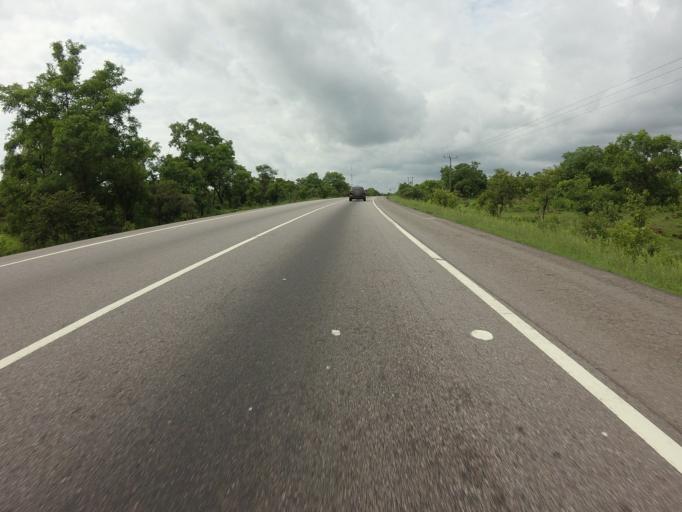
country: GH
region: Northern
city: Tamale
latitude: 8.9726
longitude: -1.3648
